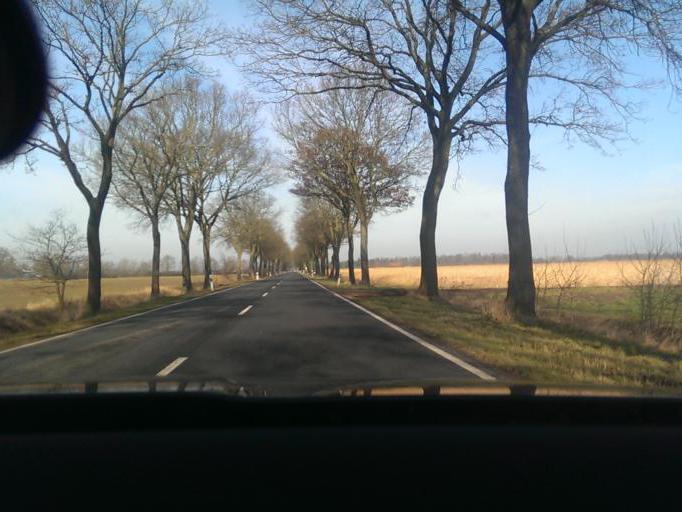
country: DE
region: Lower Saxony
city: Essel
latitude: 52.6716
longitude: 9.6571
